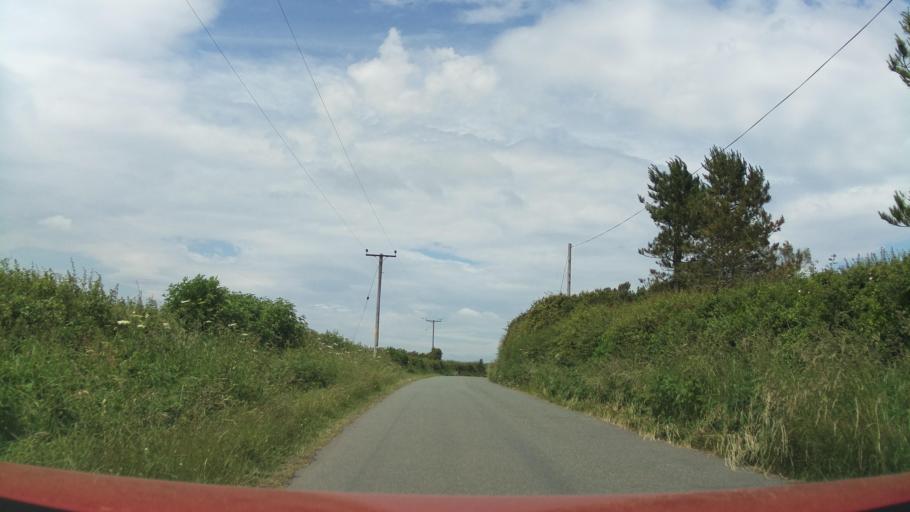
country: GB
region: Wales
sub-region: Vale of Glamorgan
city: Wick
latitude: 51.4361
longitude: -3.5668
